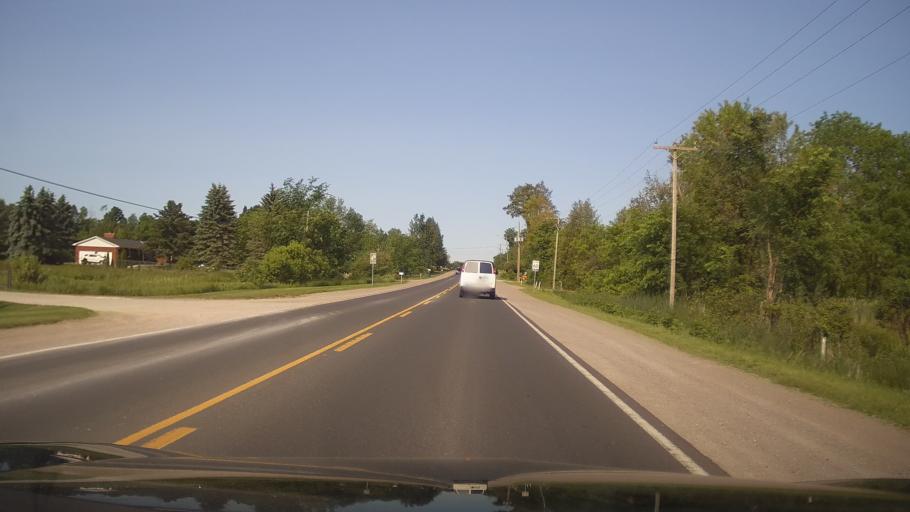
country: CA
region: Ontario
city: Peterborough
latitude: 44.2697
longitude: -78.3971
